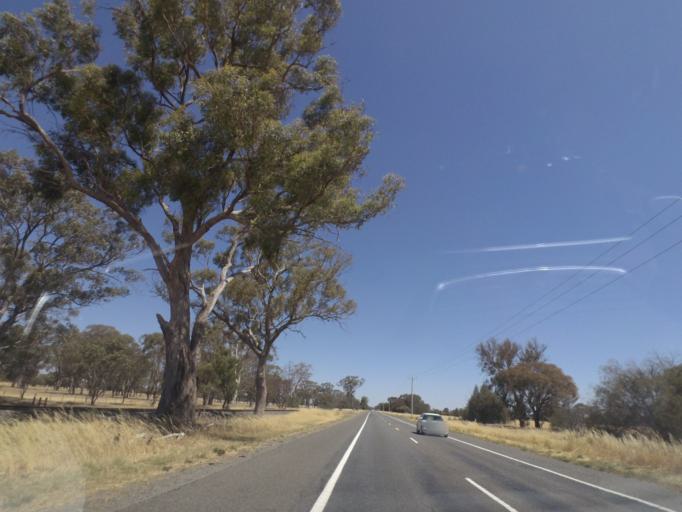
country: AU
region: Victoria
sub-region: Greater Shepparton
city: Shepparton
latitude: -36.2094
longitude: 145.4319
